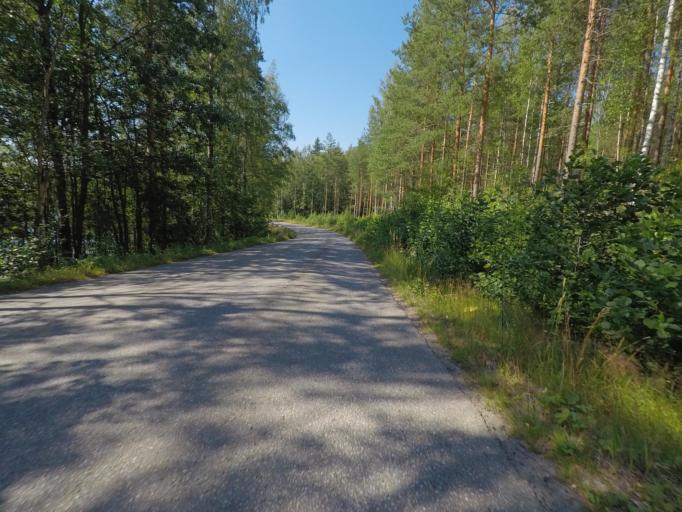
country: FI
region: Southern Savonia
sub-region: Mikkeli
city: Puumala
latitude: 61.4232
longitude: 28.1004
